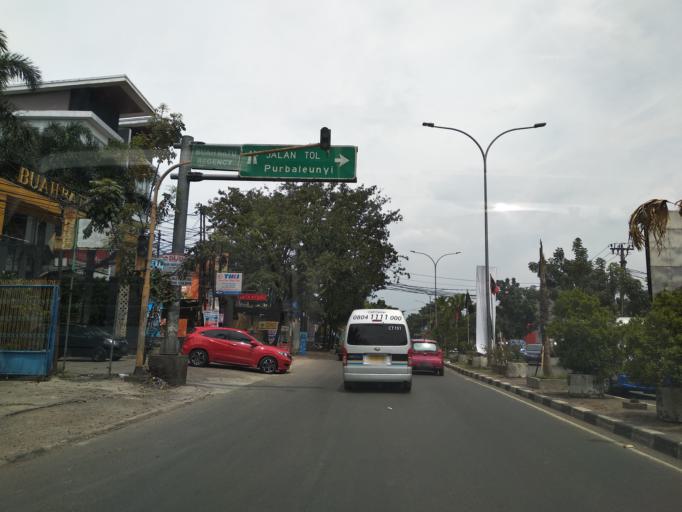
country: ID
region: West Java
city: Bandung
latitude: -6.9601
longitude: 107.6391
